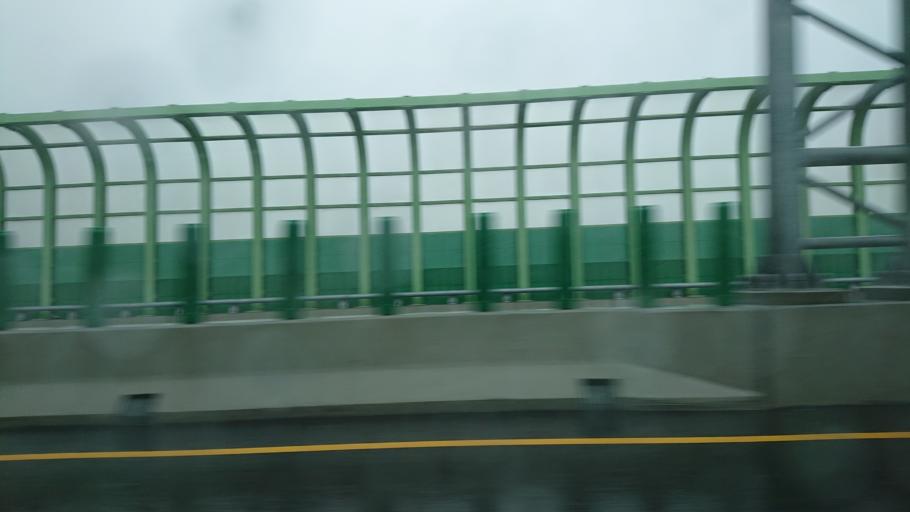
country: TW
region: Taiwan
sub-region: Changhua
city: Chang-hua
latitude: 23.9276
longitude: 120.3142
